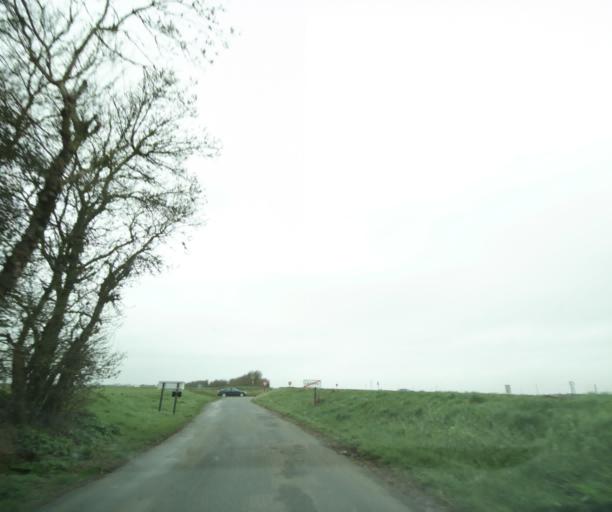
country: FR
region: Poitou-Charentes
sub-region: Departement de la Charente-Maritime
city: Puilboreau
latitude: 46.1889
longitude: -1.1327
